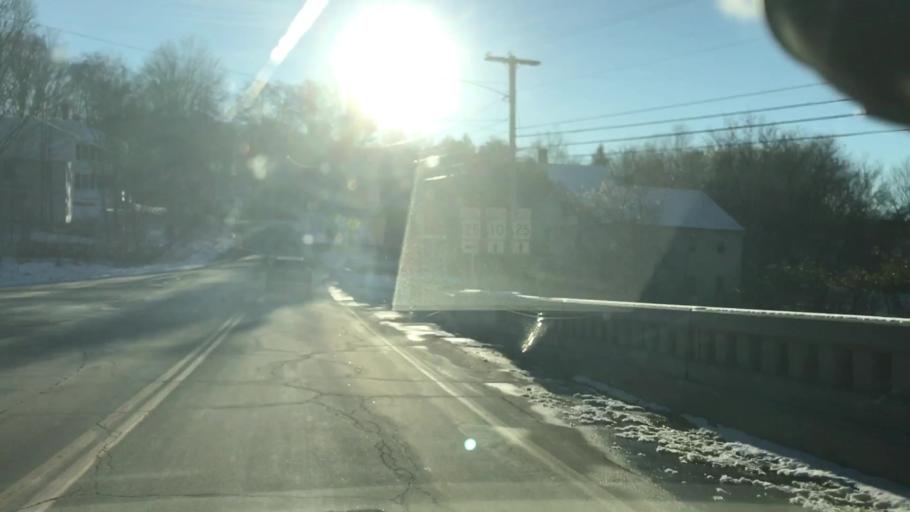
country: US
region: New Hampshire
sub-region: Grafton County
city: Haverhill
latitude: 44.0433
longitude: -72.0578
